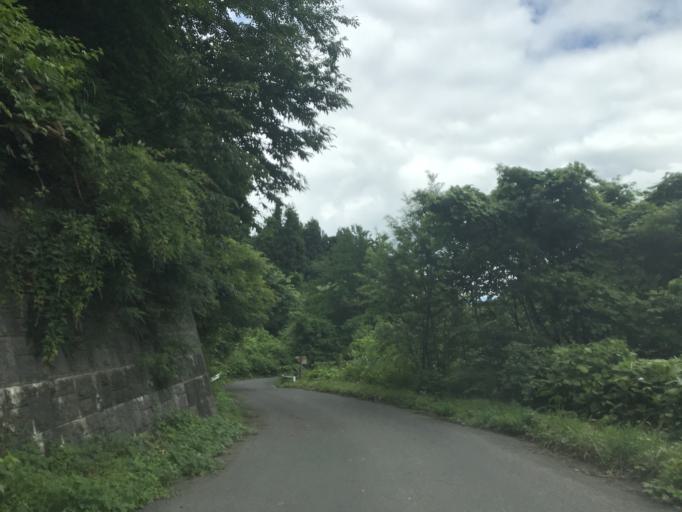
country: JP
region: Iwate
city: Ichinoseki
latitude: 38.9635
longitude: 140.9024
